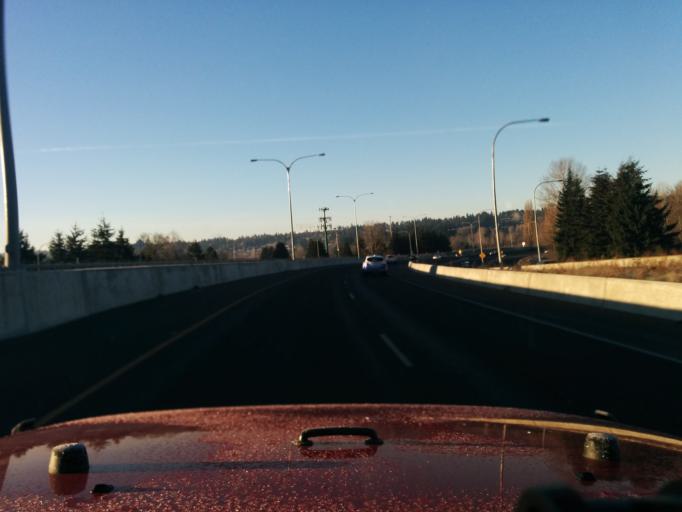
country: US
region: Washington
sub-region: King County
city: Redmond
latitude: 47.6688
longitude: -122.1084
